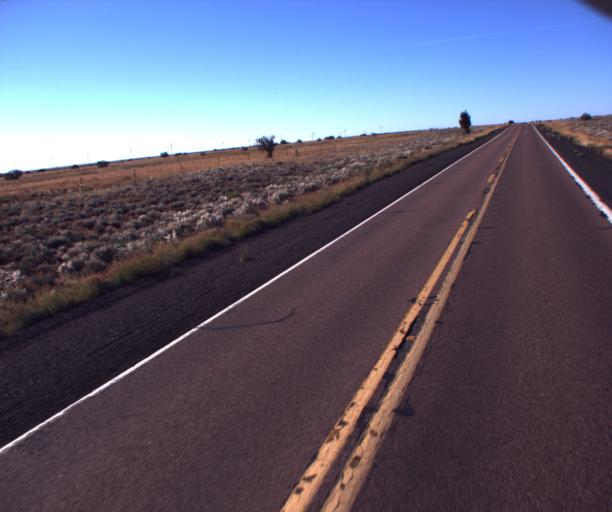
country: US
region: Arizona
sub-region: Navajo County
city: Holbrook
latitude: 34.7173
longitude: -110.2959
